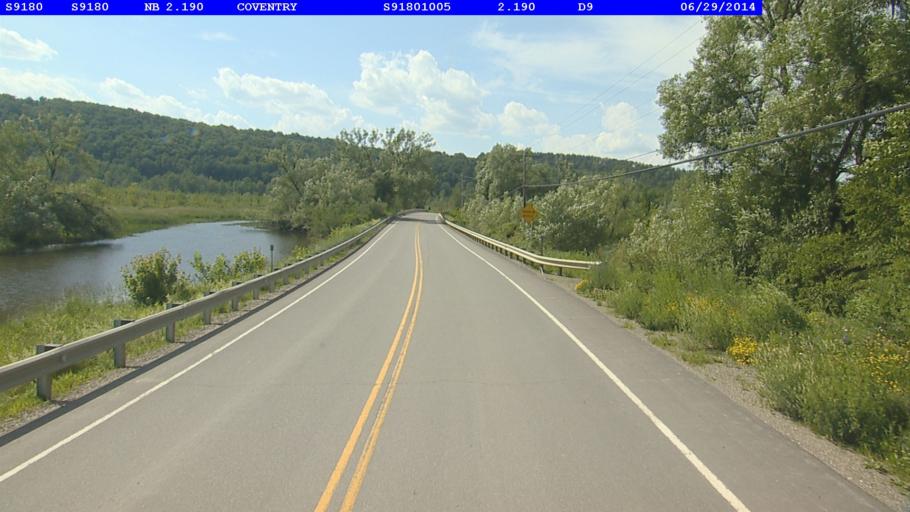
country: US
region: Vermont
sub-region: Orleans County
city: Newport
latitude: 44.9183
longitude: -72.2244
